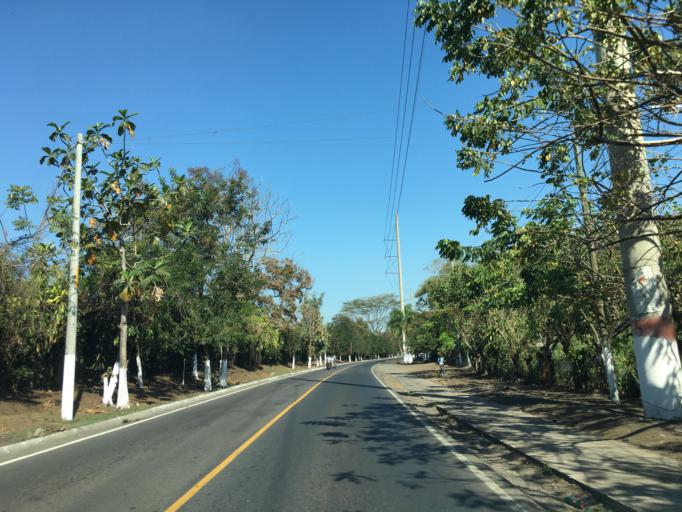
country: GT
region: Escuintla
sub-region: Municipio de La Democracia
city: La Democracia
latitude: 14.2367
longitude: -90.9533
